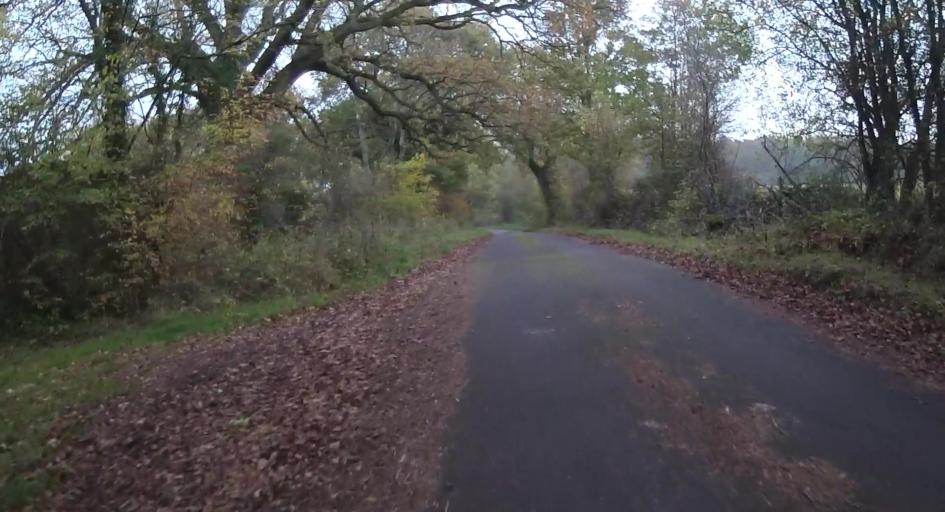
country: GB
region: England
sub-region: Surrey
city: Farnham
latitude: 51.1691
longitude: -0.8222
